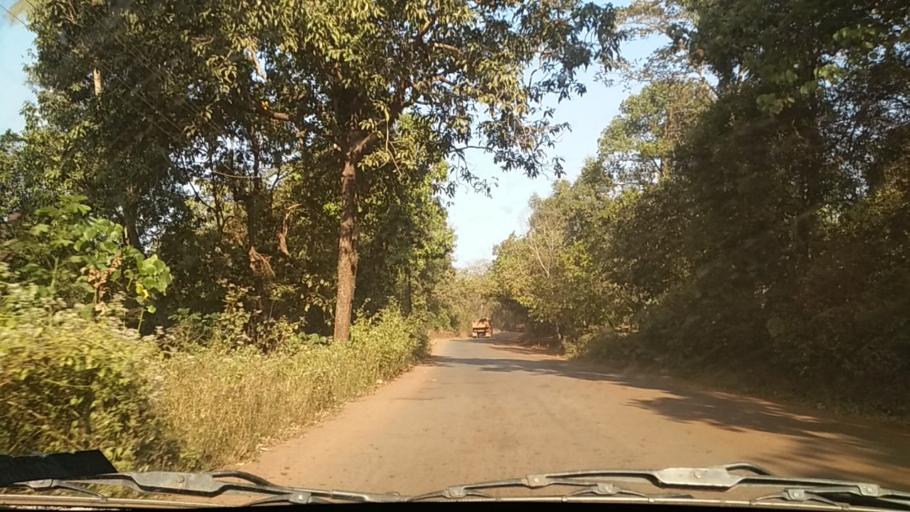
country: IN
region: Goa
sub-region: South Goa
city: Sanvordem
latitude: 15.3242
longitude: 74.1363
